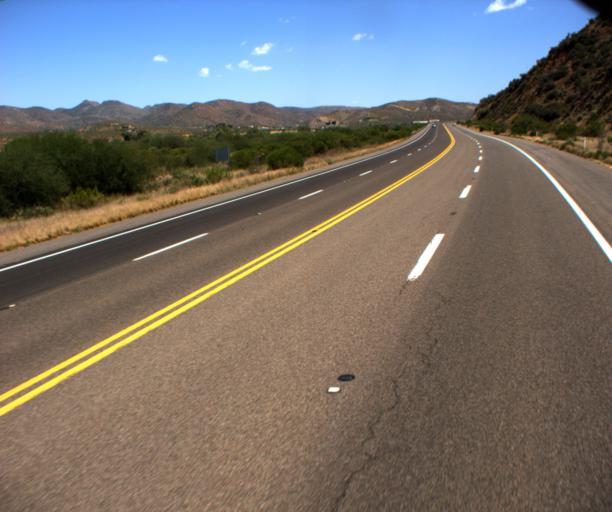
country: US
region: Arizona
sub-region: Gila County
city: Claypool
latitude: 33.4615
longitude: -110.8491
